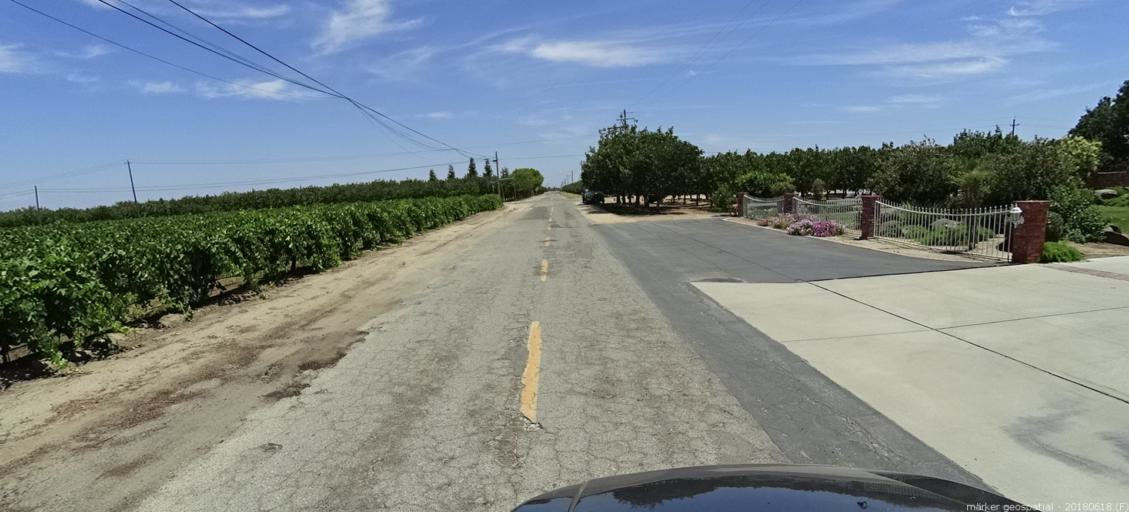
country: US
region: California
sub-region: Madera County
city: Madera
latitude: 36.9311
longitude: -120.0842
